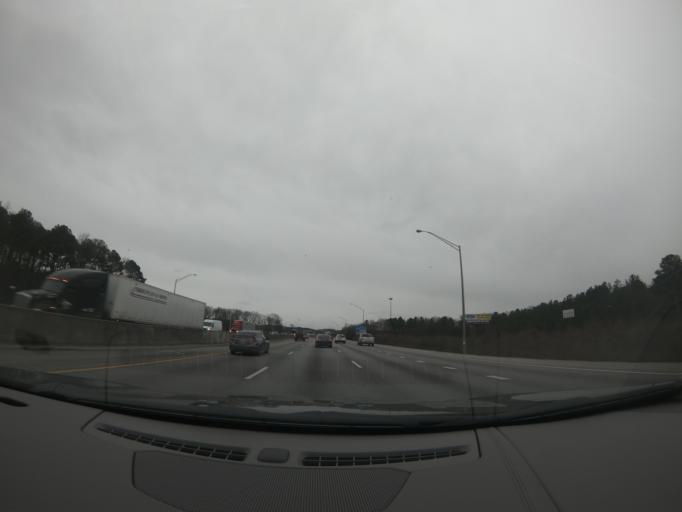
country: US
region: Tennessee
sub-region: Hamilton County
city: East Ridge
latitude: 34.9973
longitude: -85.2090
